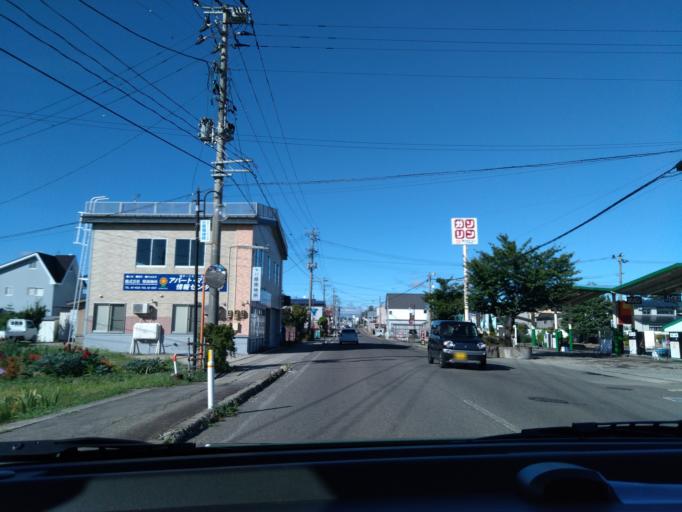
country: JP
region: Akita
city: Yuzawa
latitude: 39.2199
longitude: 140.5206
